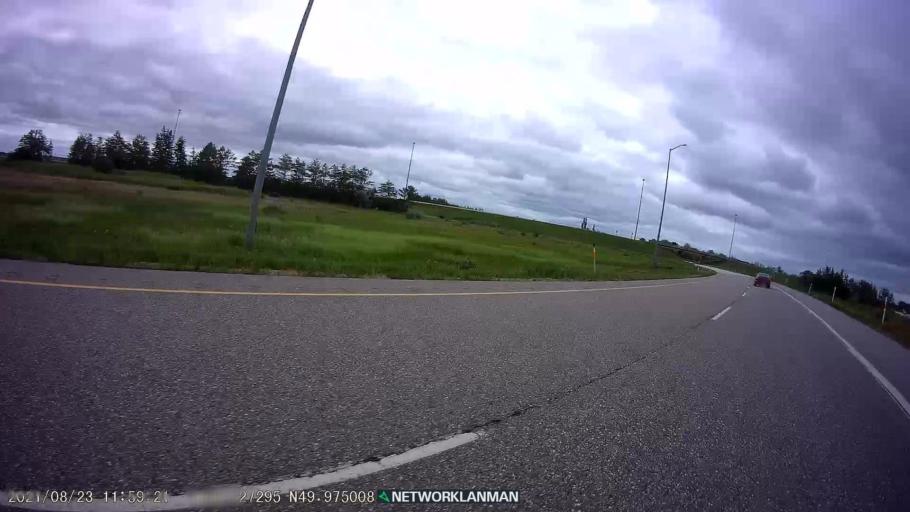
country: CA
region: Manitoba
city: Portage la Prairie
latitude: 49.9736
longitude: -98.2283
